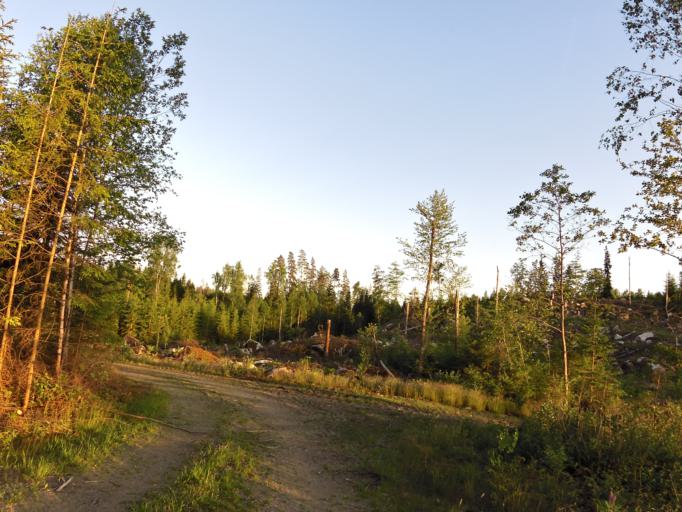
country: SE
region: Blekinge
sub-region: Olofstroms Kommun
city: Olofstroem
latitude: 56.4106
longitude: 14.5462
